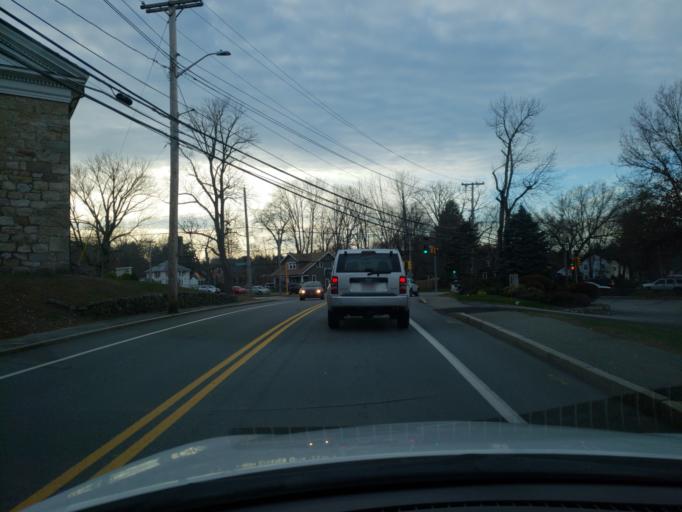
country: US
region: Massachusetts
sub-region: Essex County
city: Andover
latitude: 42.6604
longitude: -71.1656
